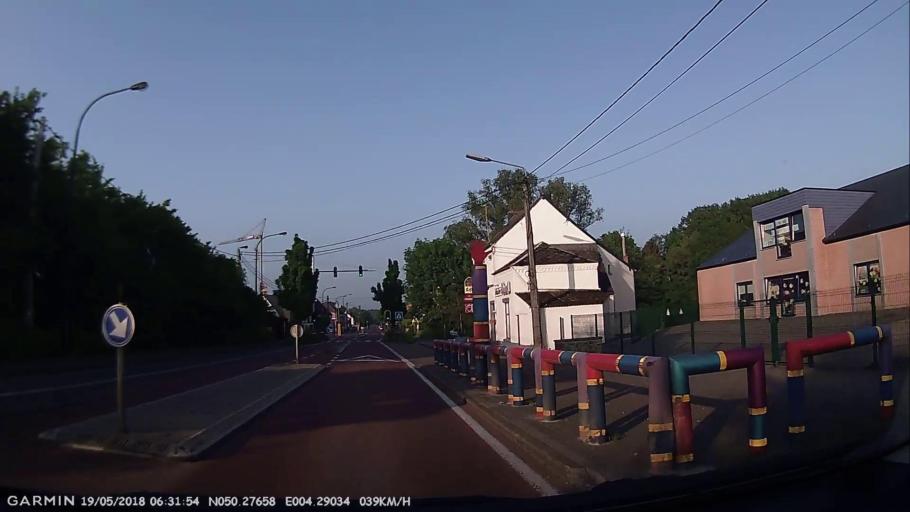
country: BE
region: Wallonia
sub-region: Province du Hainaut
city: Thuin
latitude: 50.2766
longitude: 4.2903
